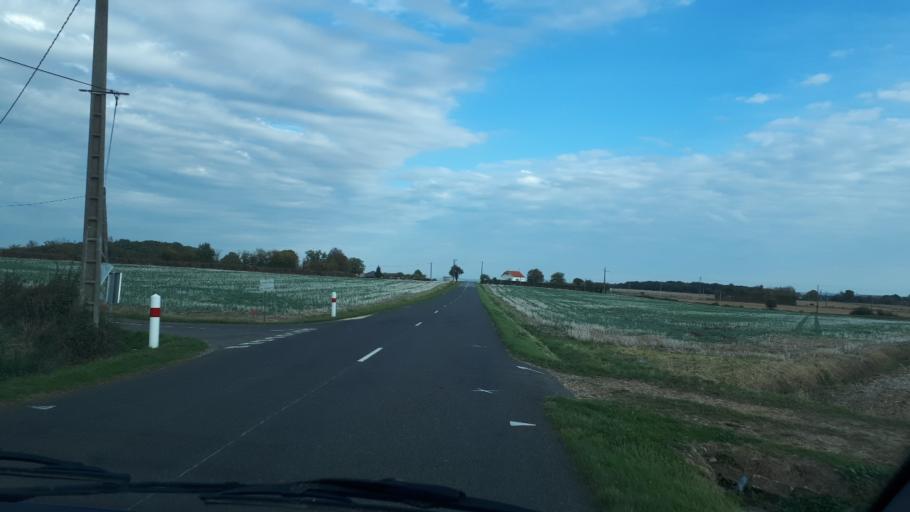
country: FR
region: Centre
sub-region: Departement du Loir-et-Cher
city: Mondoubleau
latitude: 47.9540
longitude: 0.9316
